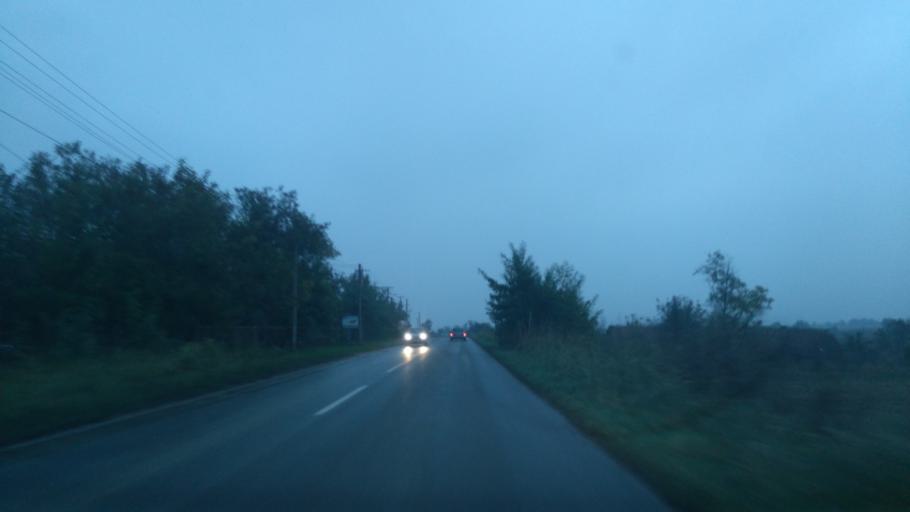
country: RS
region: Autonomna Pokrajina Vojvodina
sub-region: Juznobacki Okrug
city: Becej
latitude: 45.6490
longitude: 20.0354
